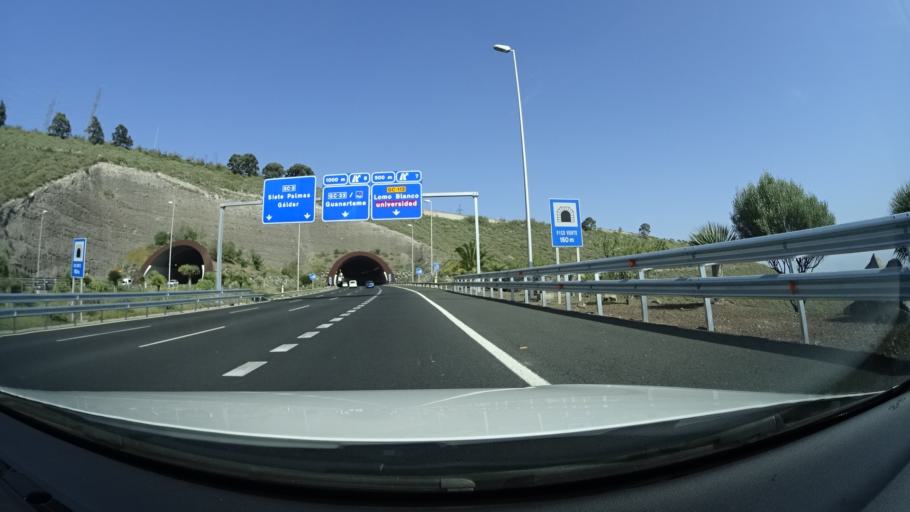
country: ES
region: Canary Islands
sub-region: Provincia de Las Palmas
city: Las Palmas de Gran Canaria
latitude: 28.0775
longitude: -15.4415
